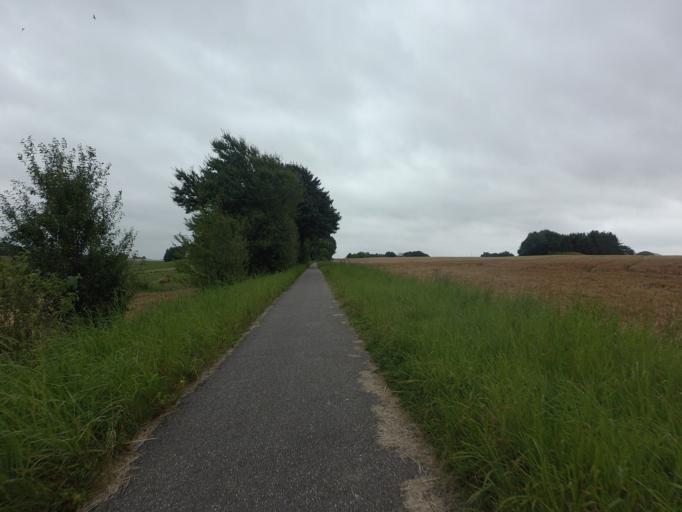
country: DK
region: Central Jutland
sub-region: Horsens Kommune
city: Braedstrup
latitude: 56.0154
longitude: 9.5837
